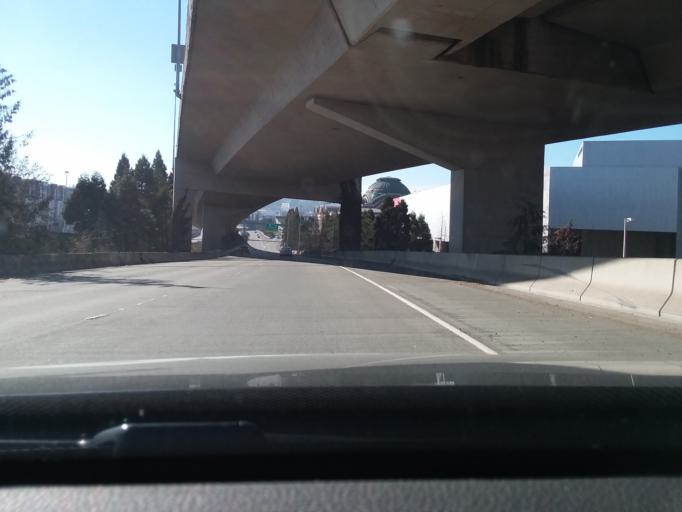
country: US
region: Washington
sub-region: Pierce County
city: Tacoma
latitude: 47.2489
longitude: -122.4360
